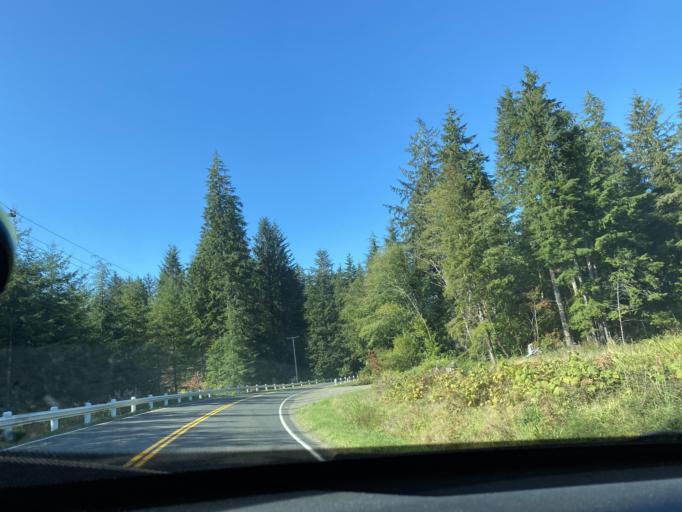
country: US
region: Washington
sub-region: Clallam County
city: Forks
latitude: 47.9515
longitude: -124.4658
